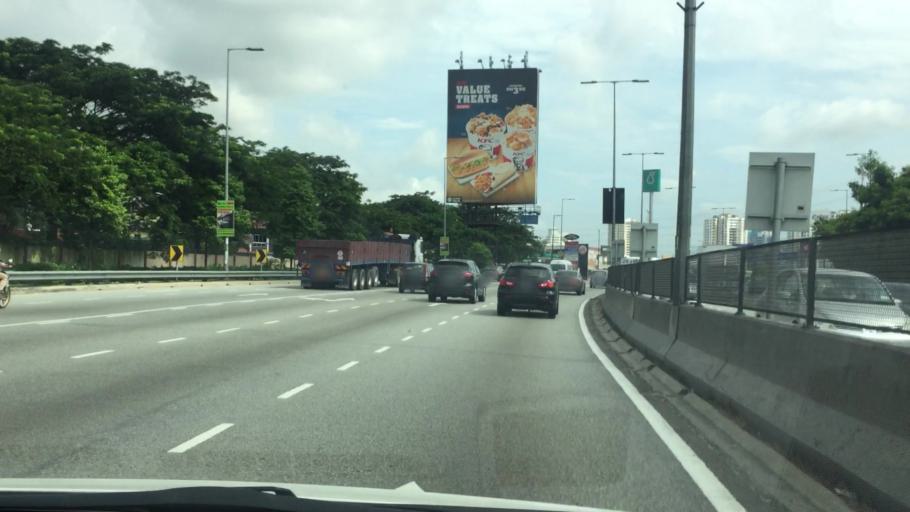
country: MY
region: Kuala Lumpur
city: Kuala Lumpur
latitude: 3.1394
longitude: 101.7431
